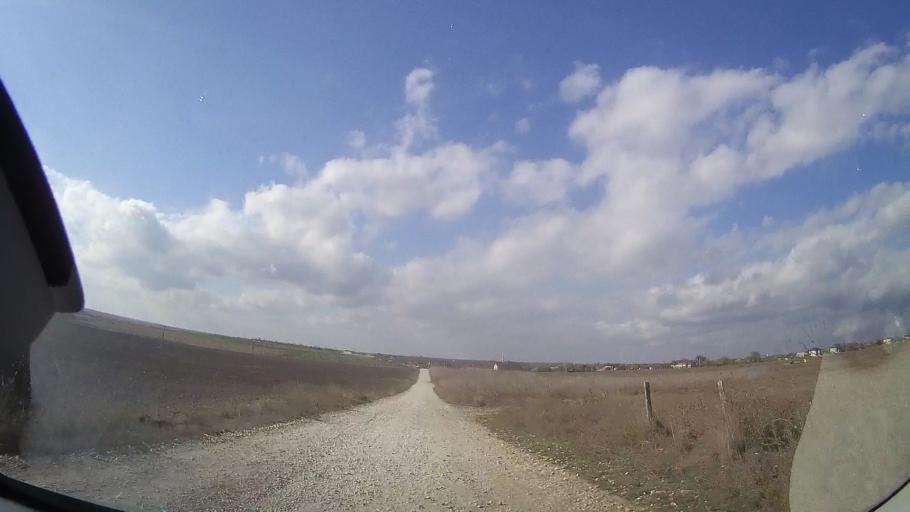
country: RO
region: Constanta
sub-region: Comuna Douazeci si Trei August
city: Douazeci si Trei August
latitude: 43.9114
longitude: 28.5943
